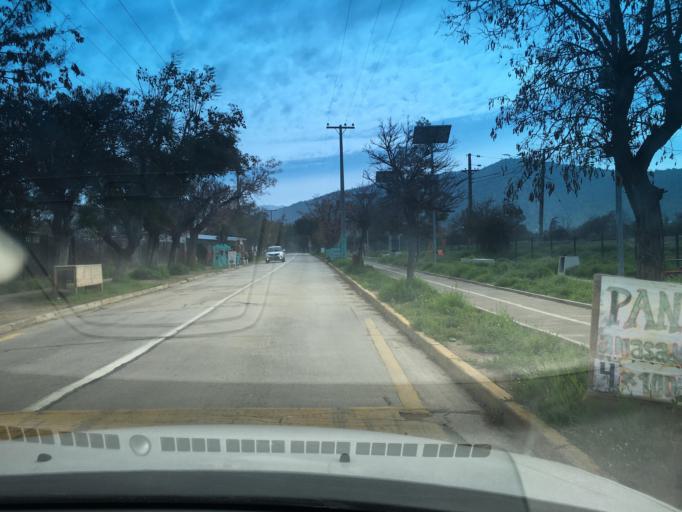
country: CL
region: Santiago Metropolitan
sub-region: Provincia de Chacabuco
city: Lampa
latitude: -33.0793
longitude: -70.9278
